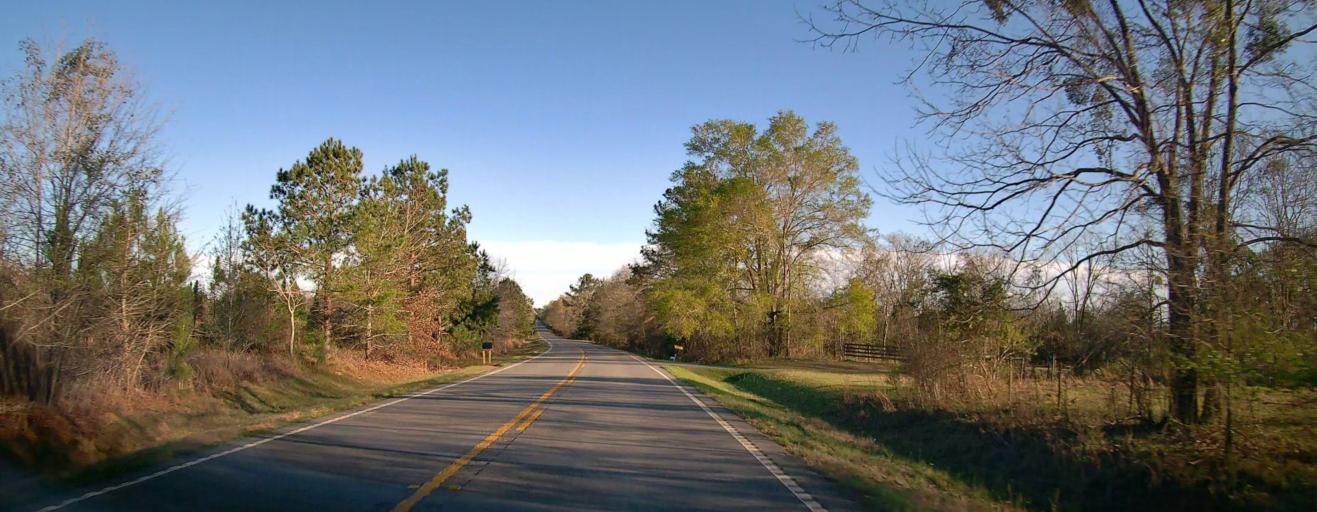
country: US
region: Georgia
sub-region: Wilcox County
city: Abbeville
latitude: 32.1230
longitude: -83.3303
